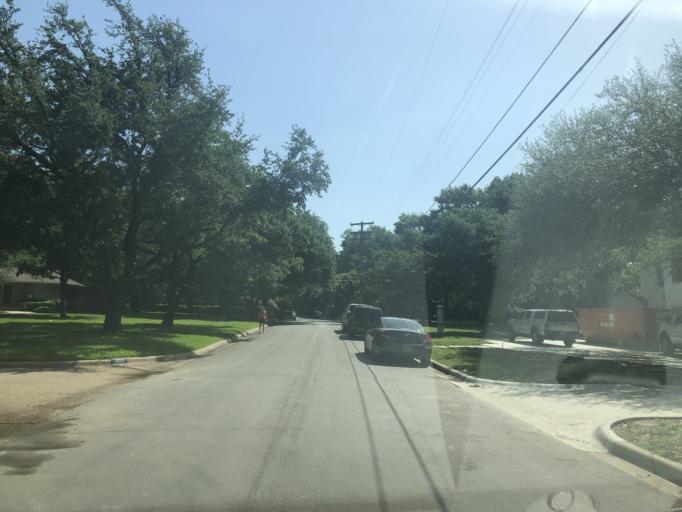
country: US
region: Texas
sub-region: Dallas County
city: University Park
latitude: 32.8821
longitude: -96.8188
